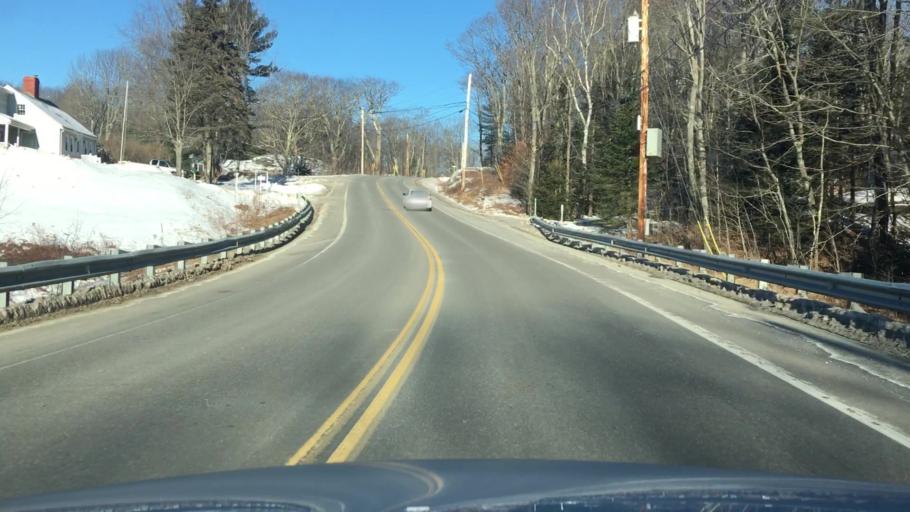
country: US
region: Maine
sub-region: Cumberland County
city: Freeport
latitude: 43.8992
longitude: -70.1143
